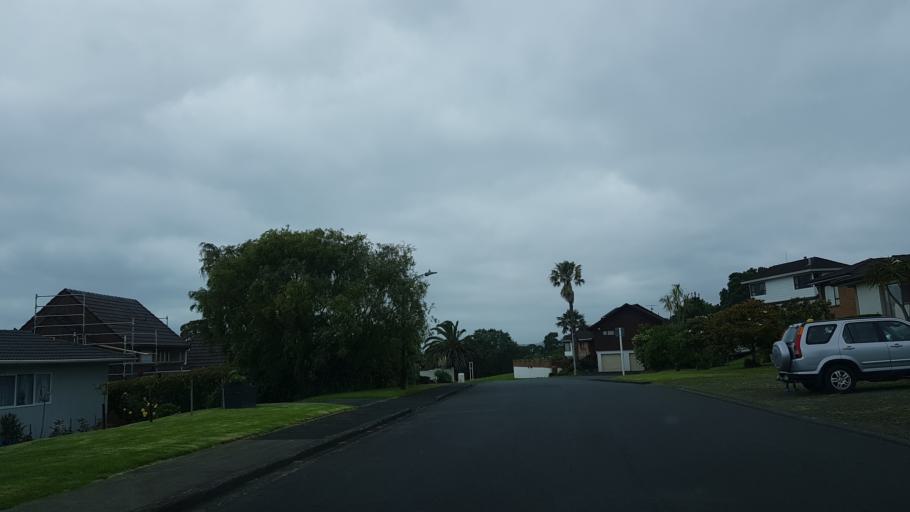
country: NZ
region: Auckland
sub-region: Auckland
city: North Shore
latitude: -36.8094
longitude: 174.7479
